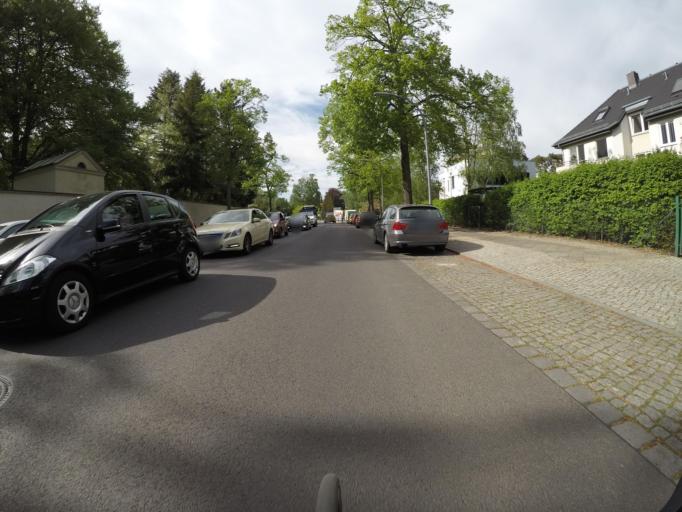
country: DE
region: Berlin
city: Lichterfelde
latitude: 52.4232
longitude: 13.2972
